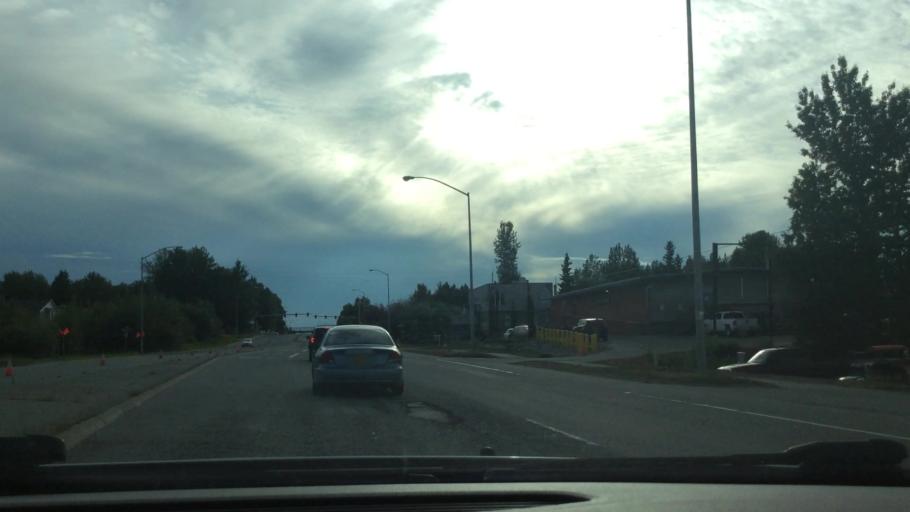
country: US
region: Alaska
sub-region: Anchorage Municipality
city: Anchorage
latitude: 61.1809
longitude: -149.8922
